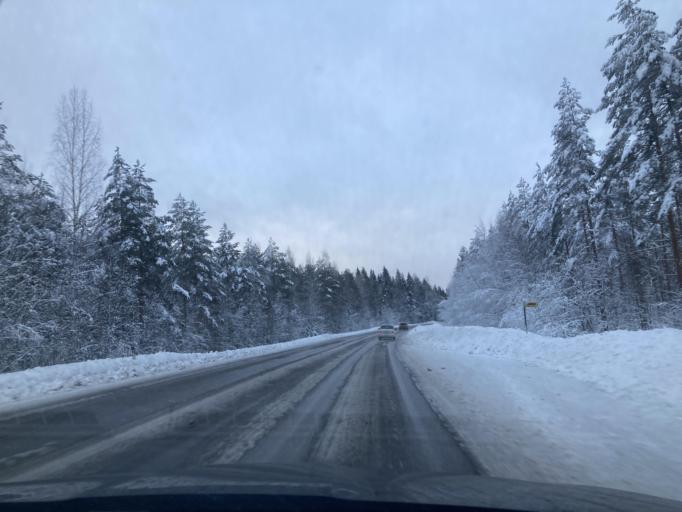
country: FI
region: Central Finland
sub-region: Jaemsae
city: Kuhmoinen
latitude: 61.4367
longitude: 25.1837
